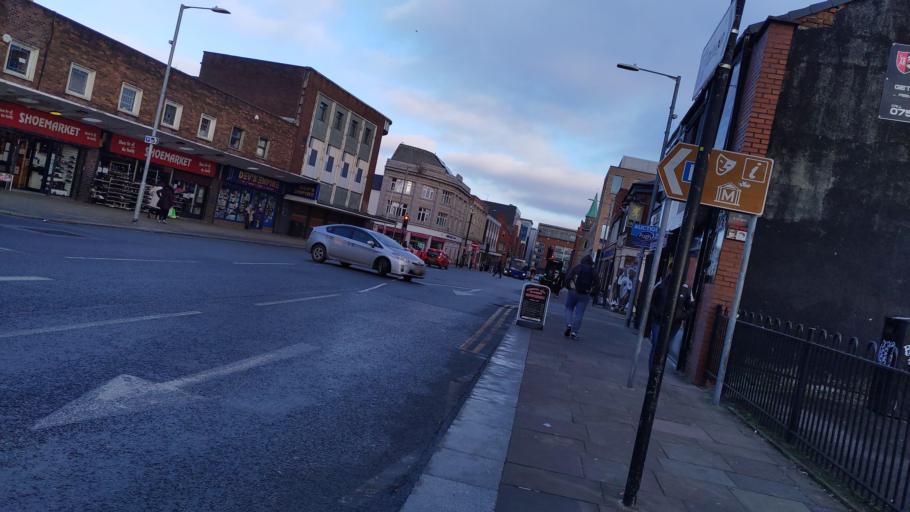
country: GB
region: England
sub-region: Borough of Bolton
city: Bolton
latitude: 53.5761
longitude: -2.4300
